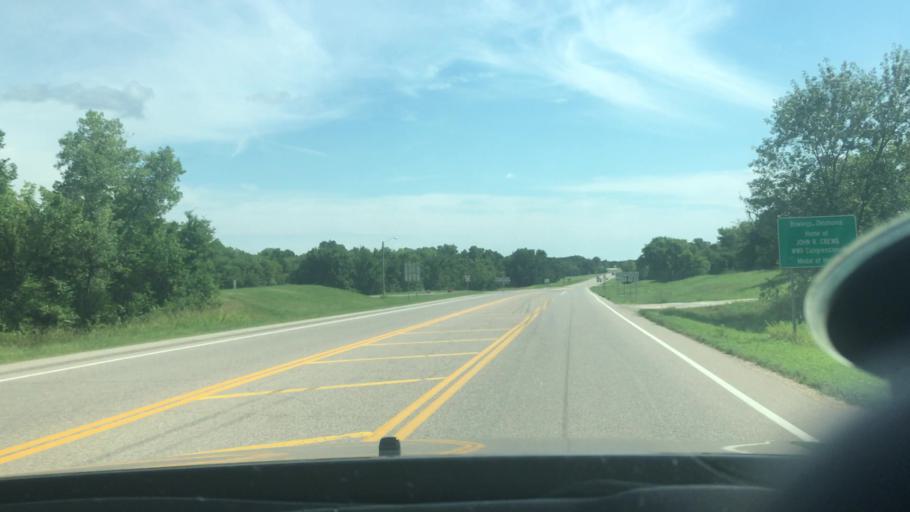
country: US
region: Oklahoma
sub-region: Seminole County
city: Seminole
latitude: 35.1504
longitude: -96.6749
